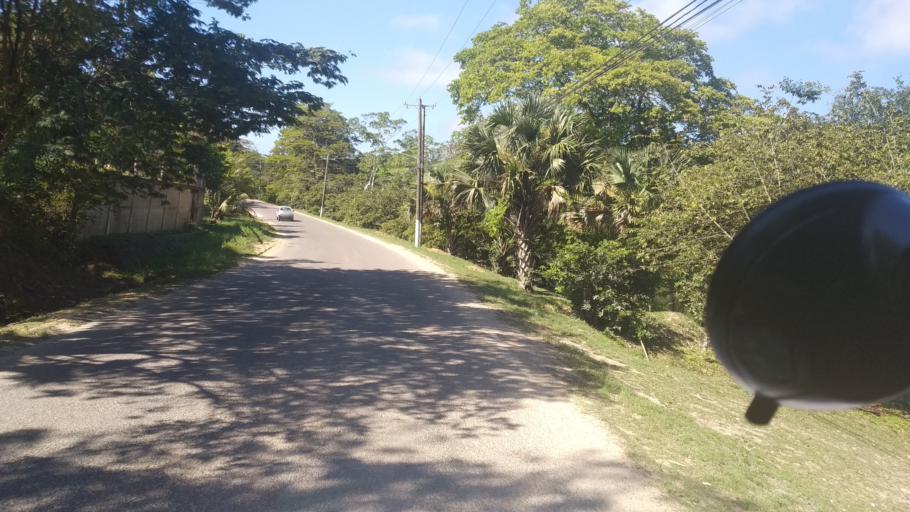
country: BZ
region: Cayo
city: Benque Viejo del Carmen
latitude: 17.0855
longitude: -89.1335
